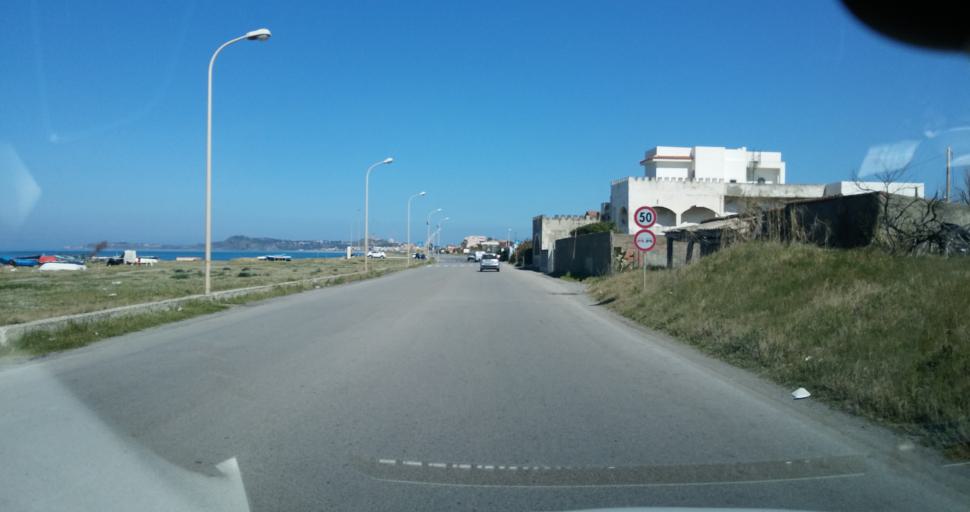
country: IT
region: Sicily
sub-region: Messina
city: Barcellona Pozzo di Gotto
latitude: 38.1857
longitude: 15.2132
